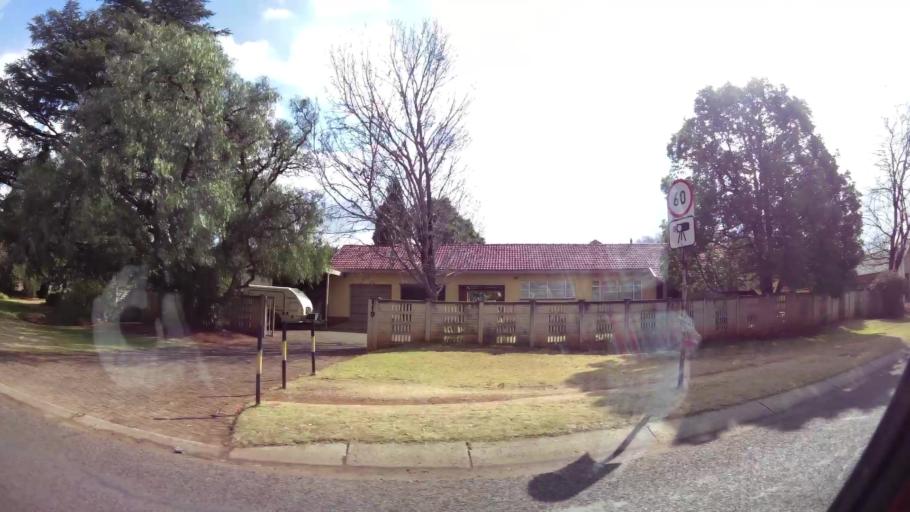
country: ZA
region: Gauteng
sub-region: Sedibeng District Municipality
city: Vanderbijlpark
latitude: -26.7364
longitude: 27.8259
